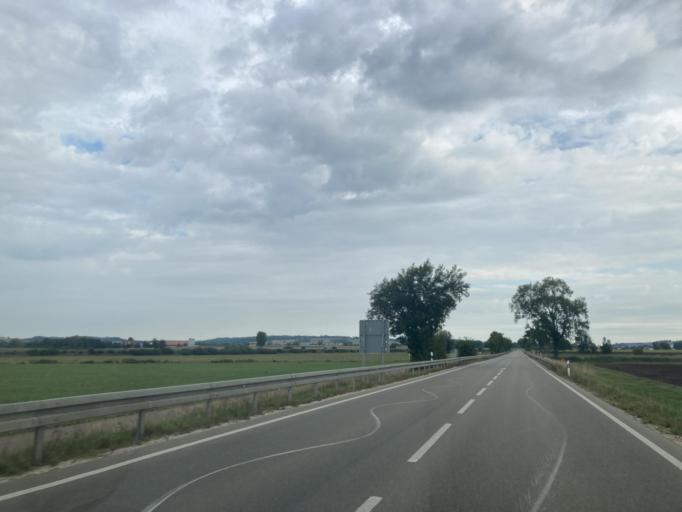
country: DE
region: Bavaria
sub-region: Swabia
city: Munningen
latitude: 48.9287
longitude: 10.5803
